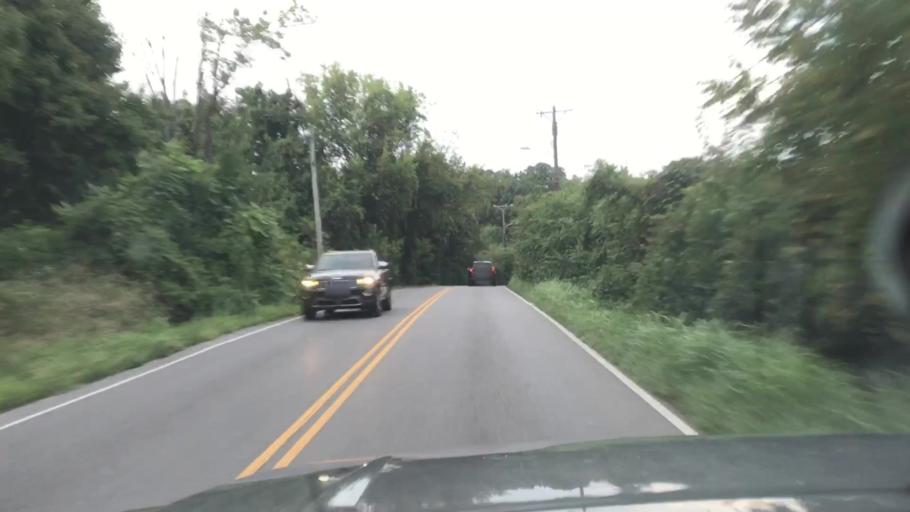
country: US
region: Tennessee
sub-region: Rutherford County
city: La Vergne
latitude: 36.0495
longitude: -86.6260
